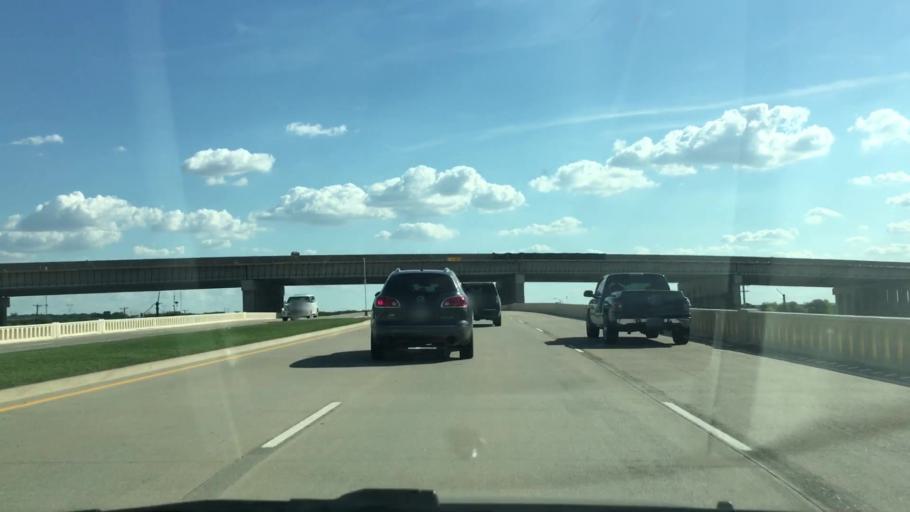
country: US
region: Texas
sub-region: Collin County
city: Prosper
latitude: 33.2208
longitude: -96.7998
